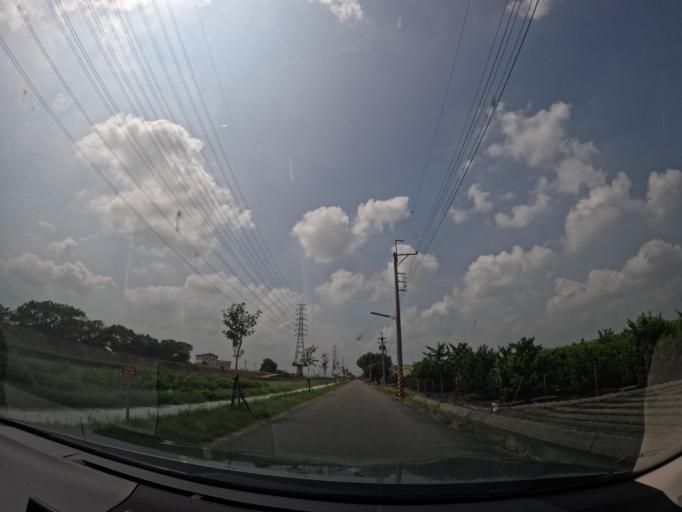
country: TW
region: Taiwan
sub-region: Yunlin
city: Douliu
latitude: 23.6680
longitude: 120.3994
